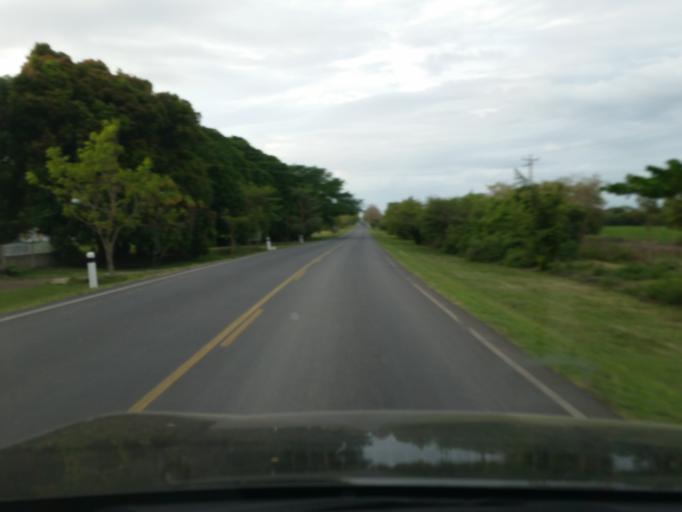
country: NI
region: Rivas
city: Belen
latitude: 11.5302
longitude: -85.8971
